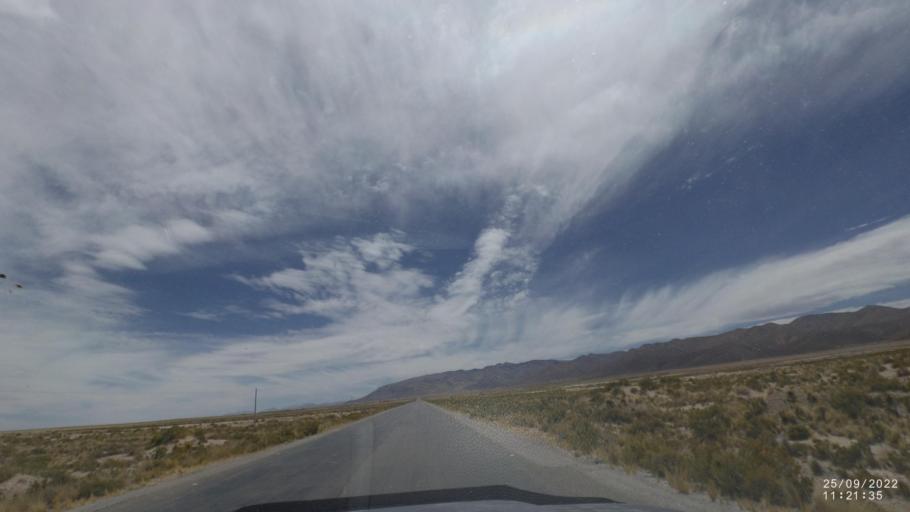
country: BO
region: Oruro
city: Challapata
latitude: -19.1410
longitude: -66.7702
